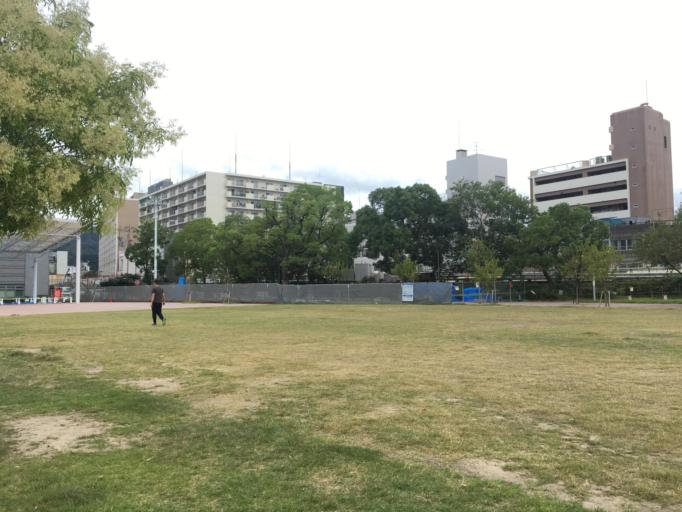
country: JP
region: Hyogo
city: Kobe
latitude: 34.6794
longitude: 135.1666
